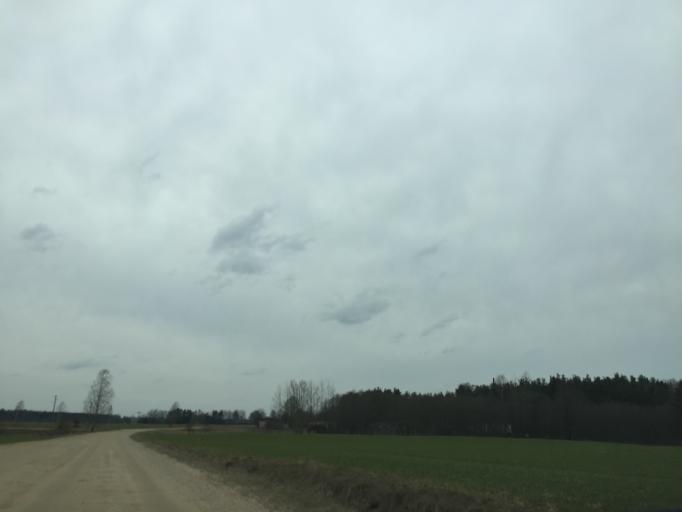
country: LV
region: Livani
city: Livani
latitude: 56.3124
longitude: 26.1614
